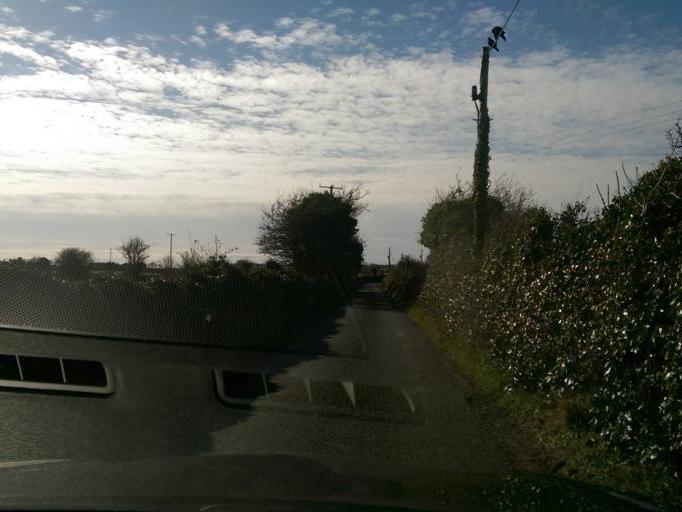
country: IE
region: Connaught
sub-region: County Galway
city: Oranmore
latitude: 53.2330
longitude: -8.9589
